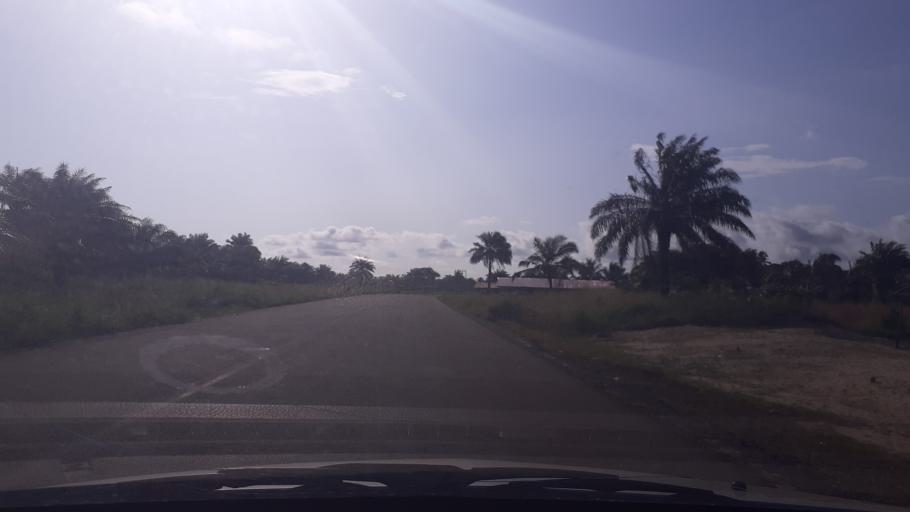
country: LR
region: Montserrado
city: Bensonville City
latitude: 6.1685
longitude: -10.4438
